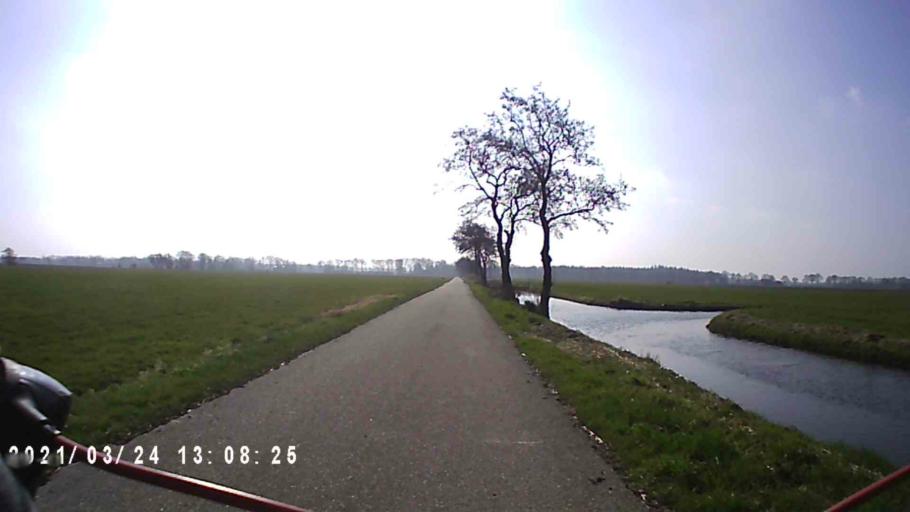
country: NL
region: Groningen
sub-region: Gemeente Leek
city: Leek
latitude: 53.1267
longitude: 6.3036
